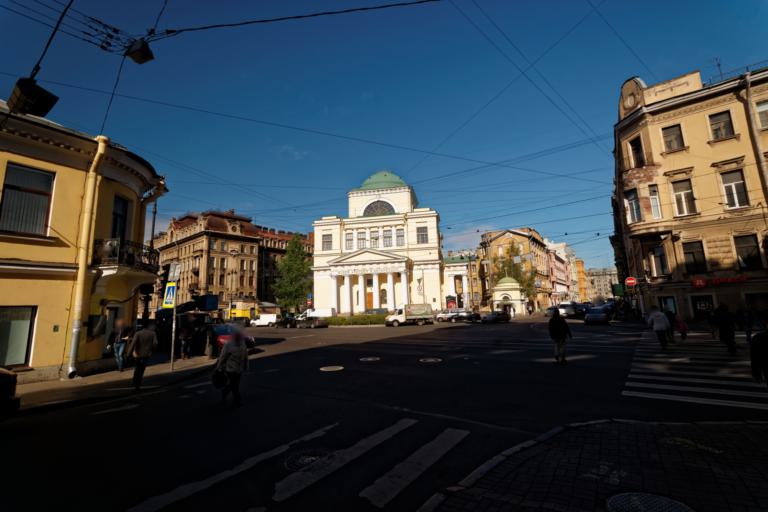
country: RU
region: St.-Petersburg
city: Centralniy
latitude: 59.9272
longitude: 30.3525
